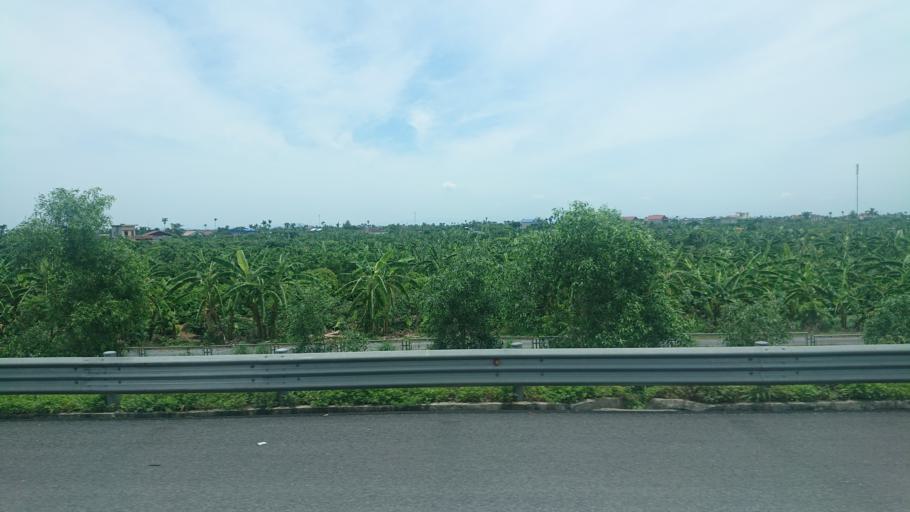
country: VN
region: Hai Duong
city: Tu Ky
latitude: 20.8212
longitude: 106.4760
